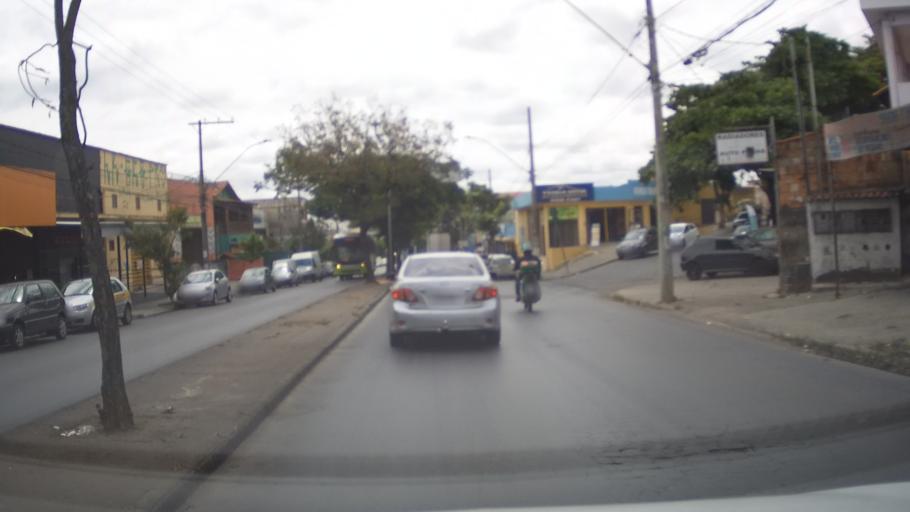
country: BR
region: Minas Gerais
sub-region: Ribeirao Das Neves
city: Ribeirao das Neves
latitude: -19.8031
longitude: -43.9960
